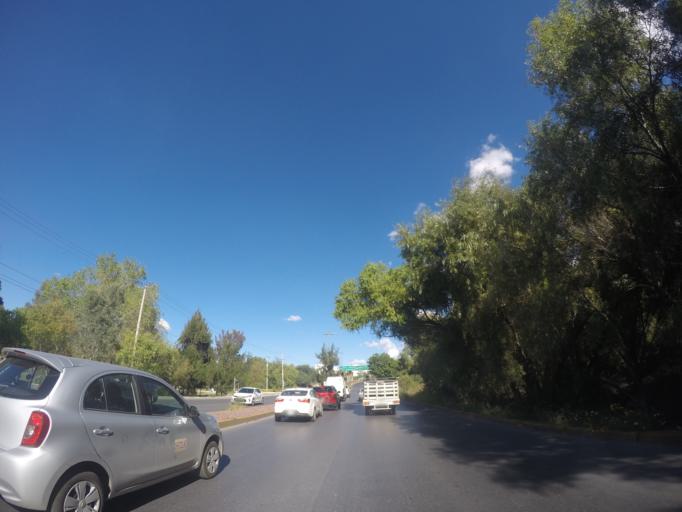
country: MX
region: San Luis Potosi
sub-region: Mexquitic de Carmona
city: Guadalupe Victoria
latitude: 22.1518
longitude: -101.0308
